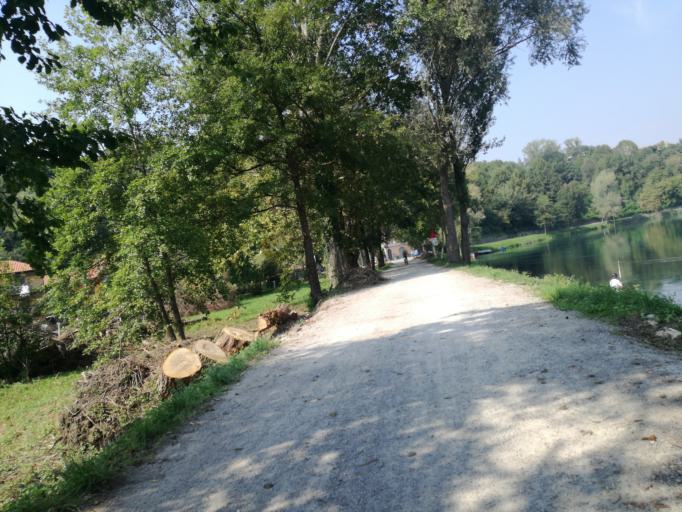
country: IT
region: Lombardy
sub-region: Provincia di Lecco
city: Brivio
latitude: 45.7320
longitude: 9.4457
